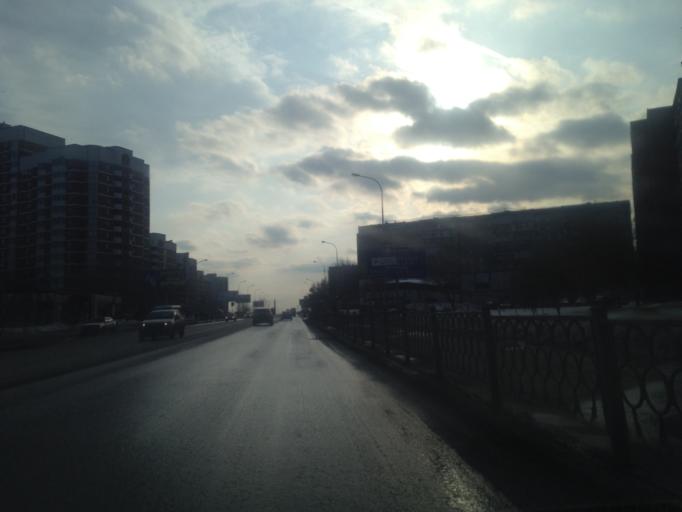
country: RU
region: Sverdlovsk
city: Yekaterinburg
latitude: 56.8530
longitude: 60.5715
